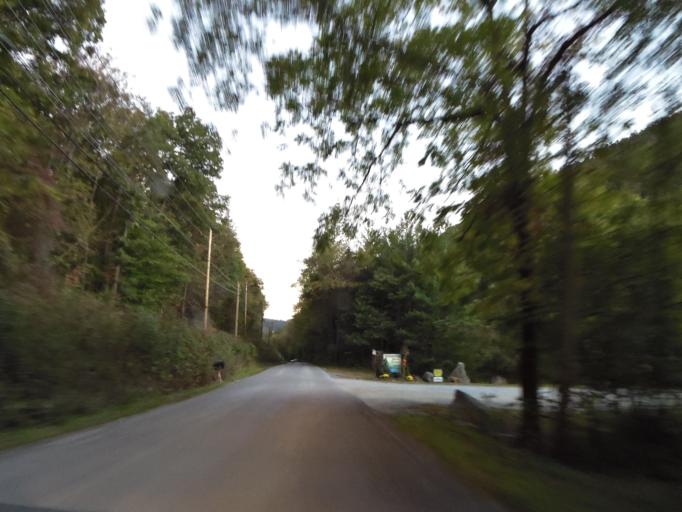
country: US
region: Tennessee
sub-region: Blount County
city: Wildwood
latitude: 35.7374
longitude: -83.8216
